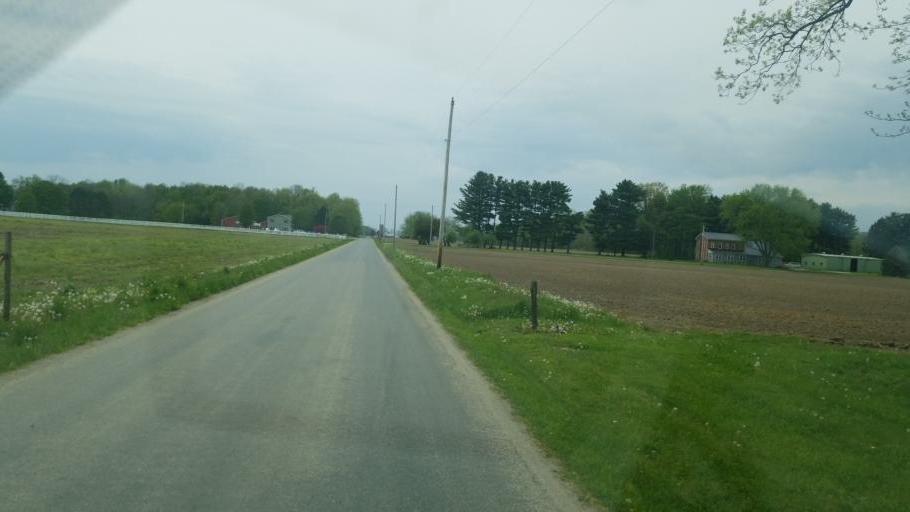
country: US
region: Ohio
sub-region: Richland County
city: Shelby
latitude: 40.9303
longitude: -82.6904
